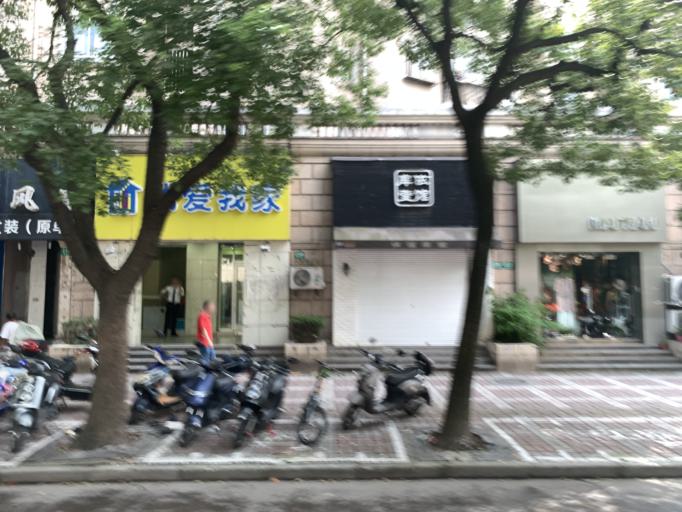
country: CN
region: Shanghai Shi
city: Pudong
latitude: 31.2481
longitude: 121.5487
